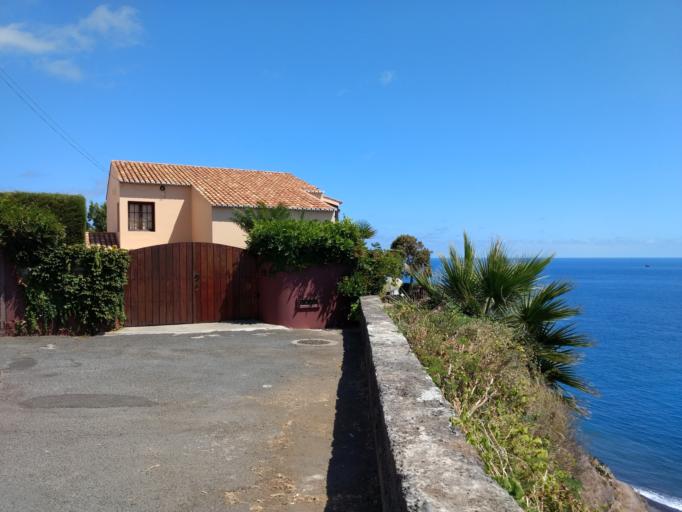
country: PT
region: Madeira
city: Camara de Lobos
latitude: 32.6430
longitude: -16.9581
